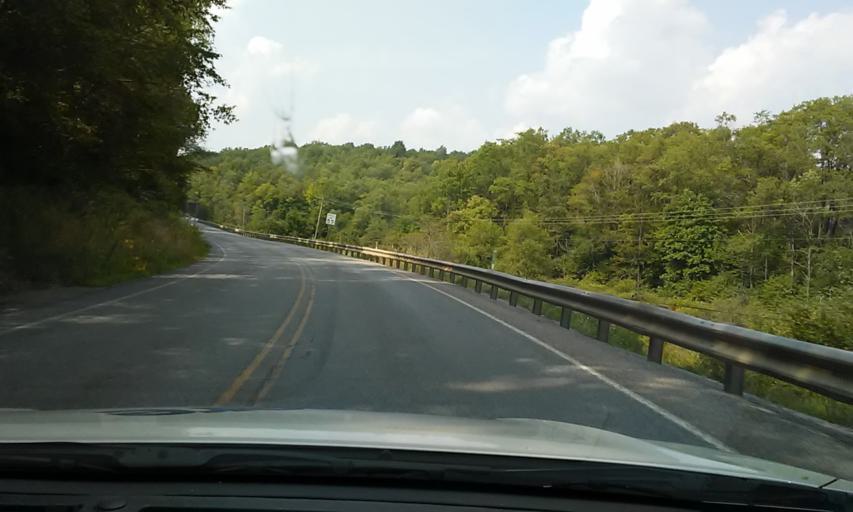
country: US
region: Pennsylvania
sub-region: Potter County
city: Coudersport
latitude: 41.8766
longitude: -77.8375
